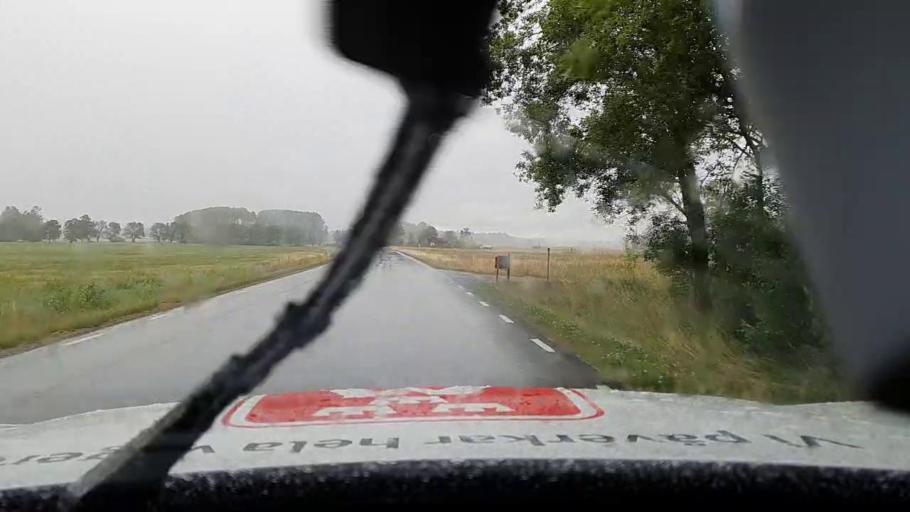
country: SE
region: Vaestra Goetaland
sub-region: Toreboda Kommun
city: Toereboda
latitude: 58.6692
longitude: 14.1325
